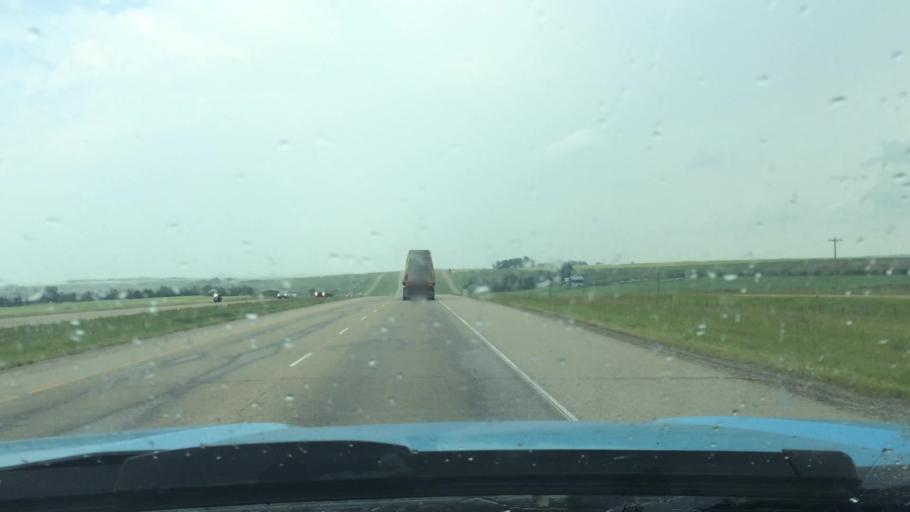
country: CA
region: Alberta
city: Carstairs
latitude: 51.5410
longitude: -114.0250
